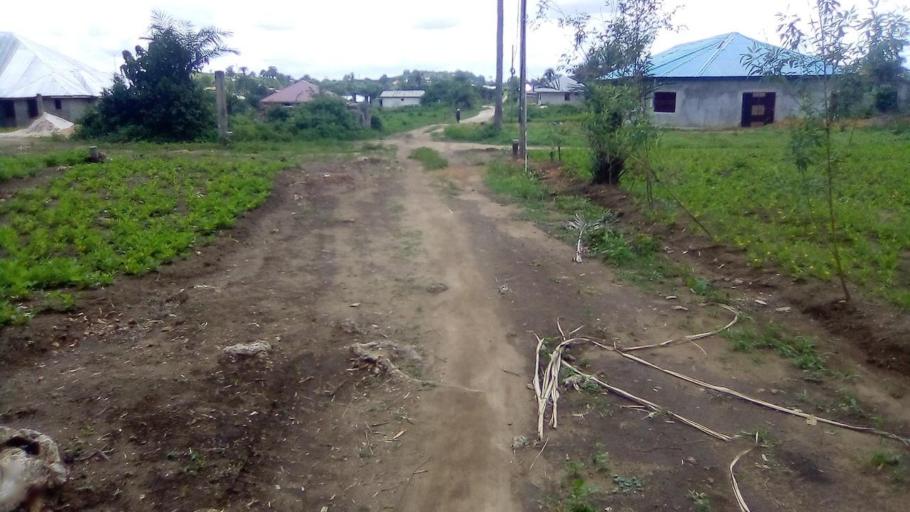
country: SL
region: Southern Province
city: Bo
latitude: 7.9324
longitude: -11.7501
